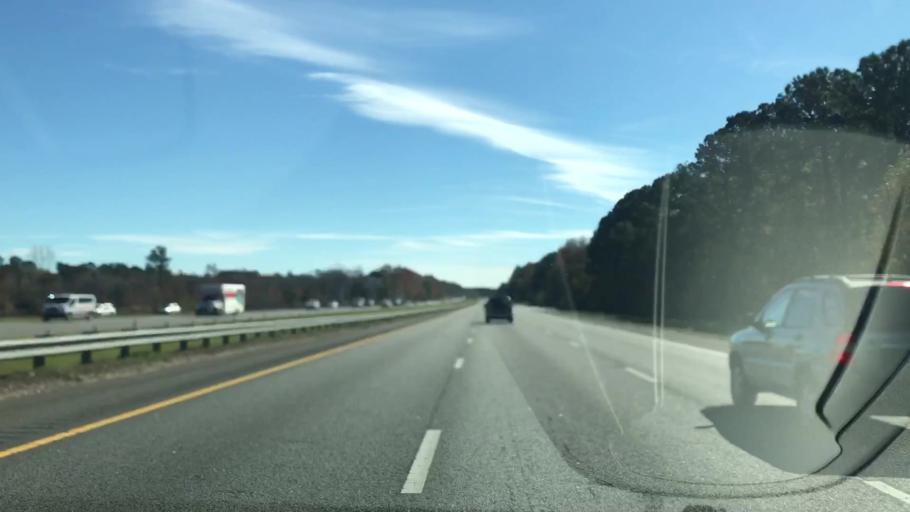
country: US
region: South Carolina
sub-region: Berkeley County
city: Ladson
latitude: 32.9974
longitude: -80.0929
